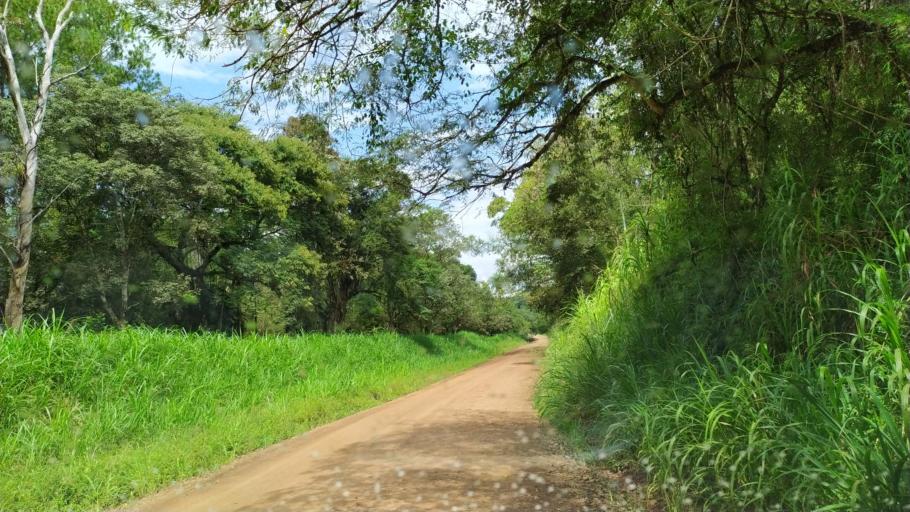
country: AR
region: Misiones
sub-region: Departamento de Eldorado
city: Eldorado
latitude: -26.4835
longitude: -54.5898
